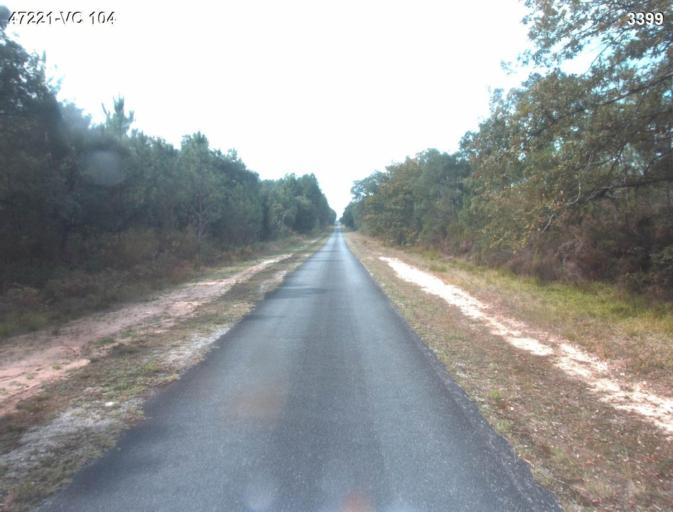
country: FR
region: Aquitaine
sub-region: Departement du Lot-et-Garonne
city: Mezin
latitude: 44.1247
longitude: 0.1867
